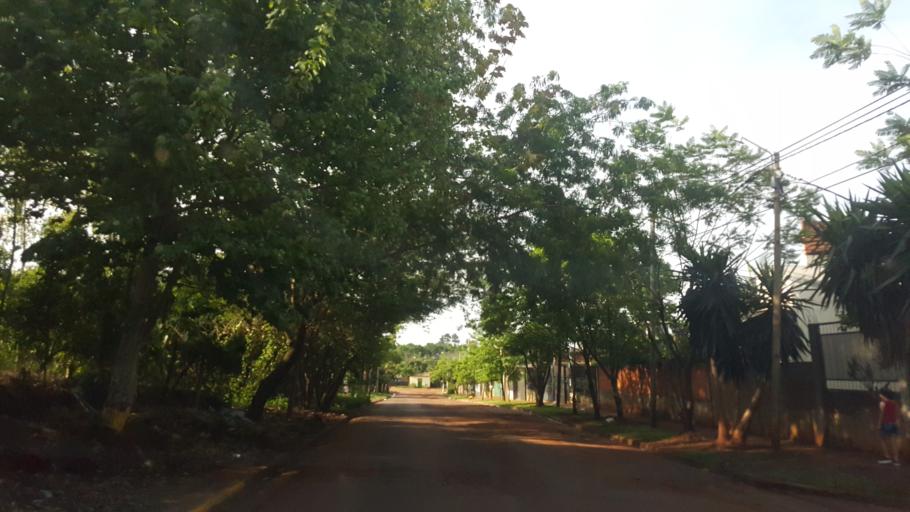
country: AR
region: Misiones
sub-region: Departamento de Capital
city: Posadas
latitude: -27.4243
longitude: -55.9245
